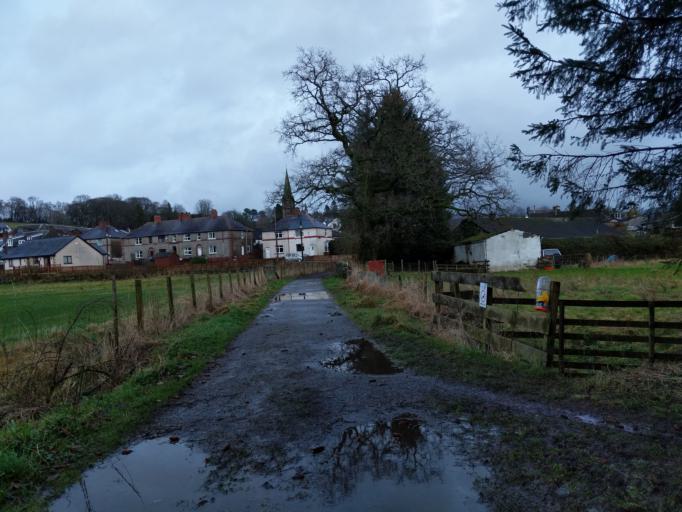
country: GB
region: Scotland
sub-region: Dumfries and Galloway
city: Moffat
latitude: 55.3346
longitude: -3.4489
